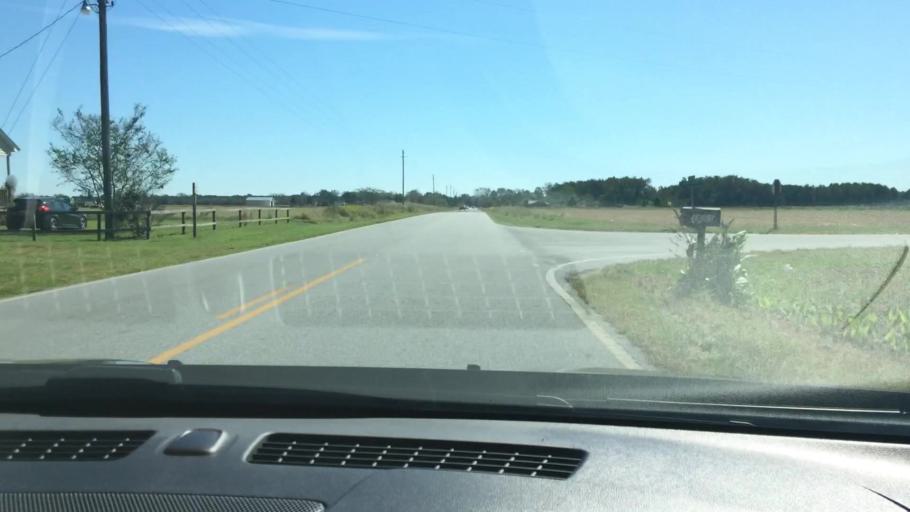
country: US
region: North Carolina
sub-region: Pitt County
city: Grifton
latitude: 35.3834
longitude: -77.3759
